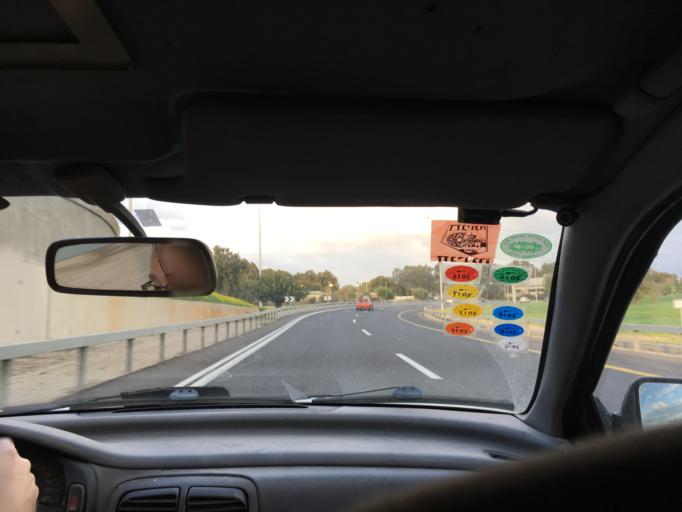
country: IL
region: Tel Aviv
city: Ramat HaSharon
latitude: 32.1373
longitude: 34.8125
